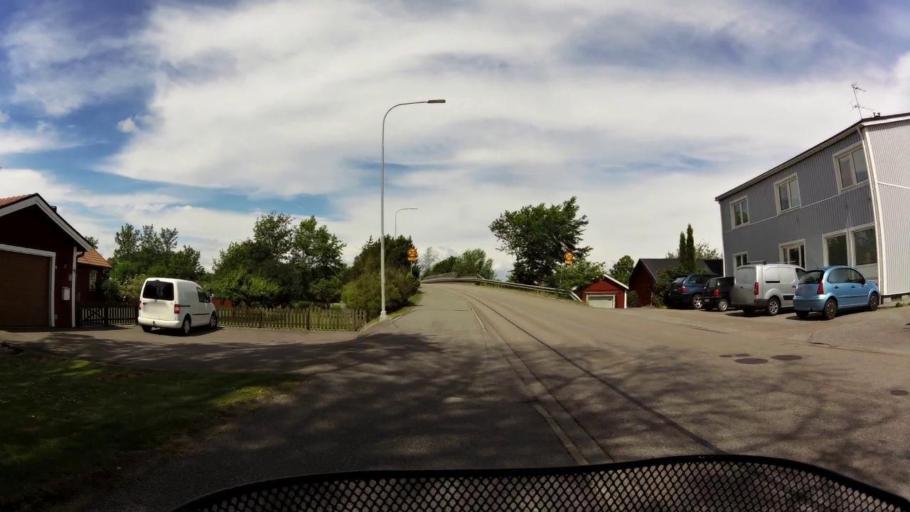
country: SE
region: OEstergoetland
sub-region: Linkopings Kommun
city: Malmslatt
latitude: 58.4107
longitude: 15.5175
